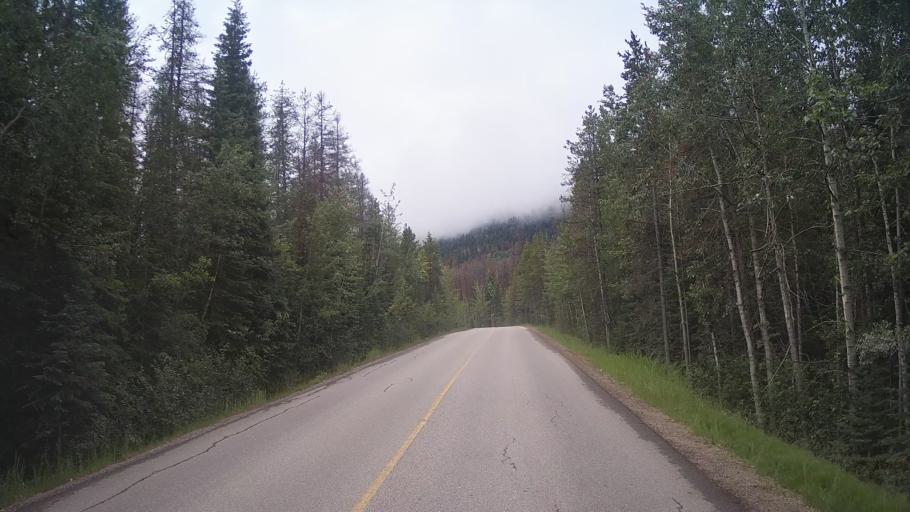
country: CA
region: Alberta
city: Jasper Park Lodge
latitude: 52.8562
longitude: -118.1030
